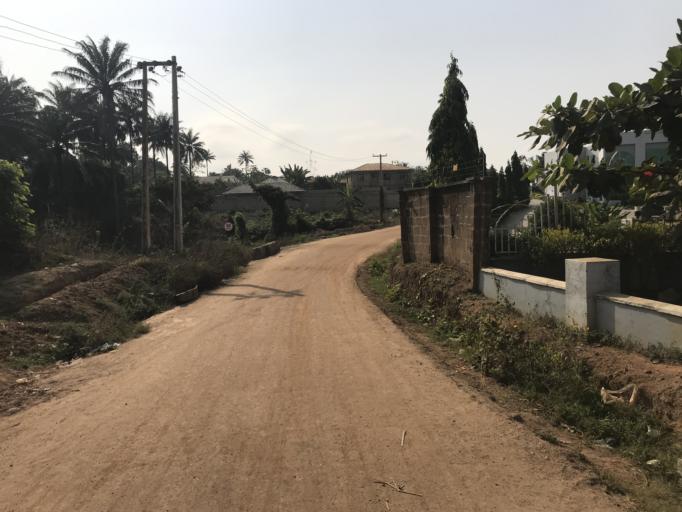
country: NG
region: Osun
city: Iwo
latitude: 7.6193
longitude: 4.1445
